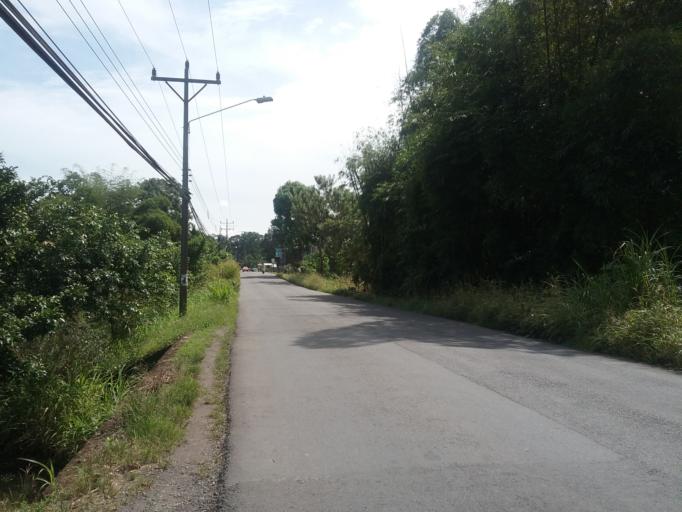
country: CR
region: Limon
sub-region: Canton de Pococi
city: Guapiles
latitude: 10.3204
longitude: -83.8961
